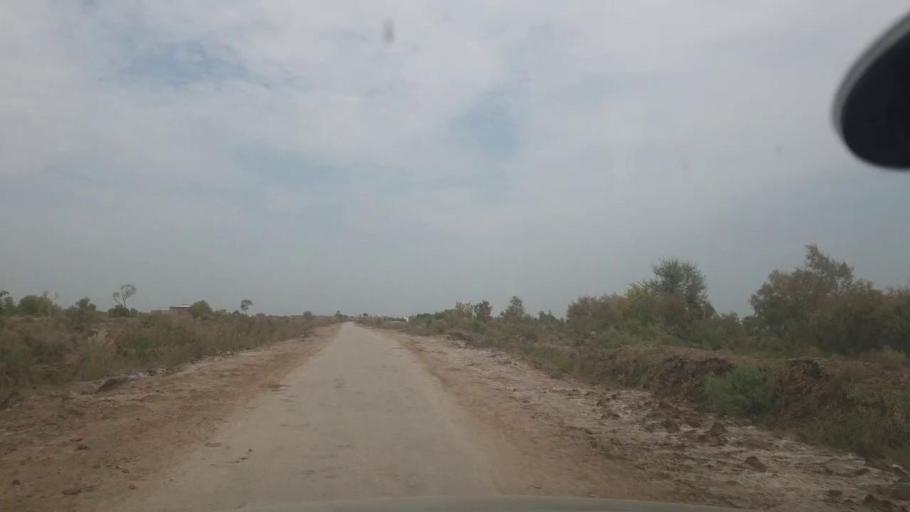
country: PK
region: Balochistan
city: Mehrabpur
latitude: 28.0551
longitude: 68.1465
